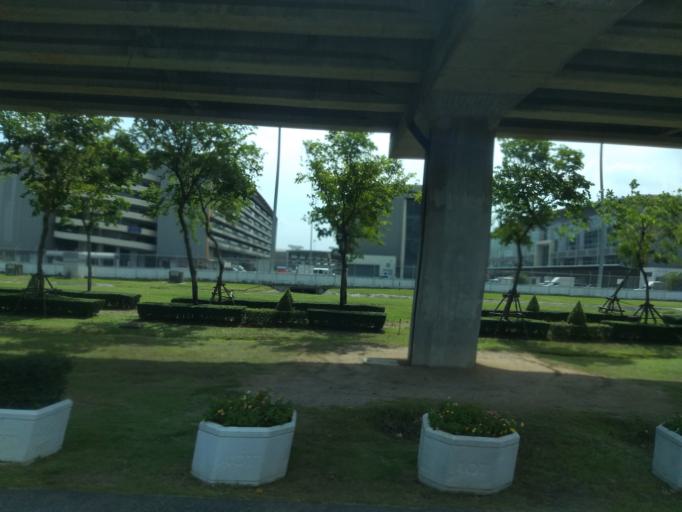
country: TH
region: Bangkok
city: Lat Krabang
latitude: 13.7105
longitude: 100.7540
